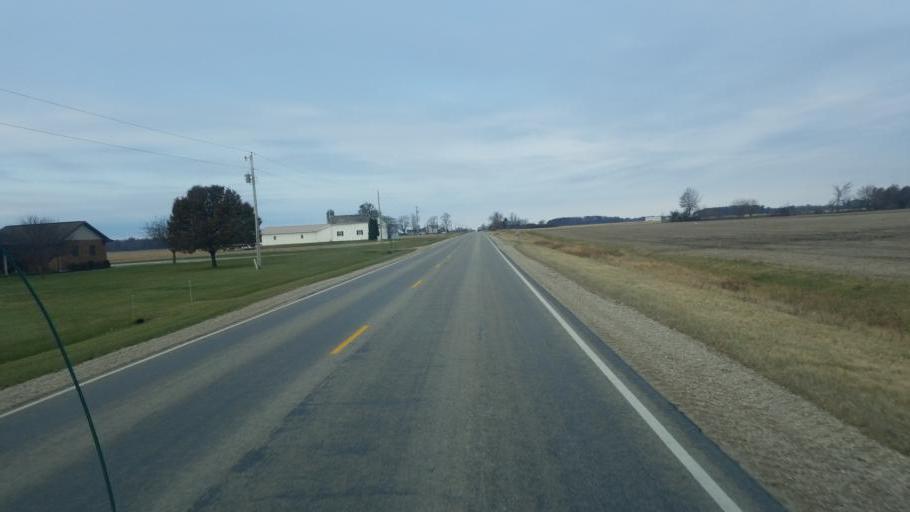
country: US
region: Indiana
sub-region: Adams County
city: Geneva
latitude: 40.5425
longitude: -84.8616
